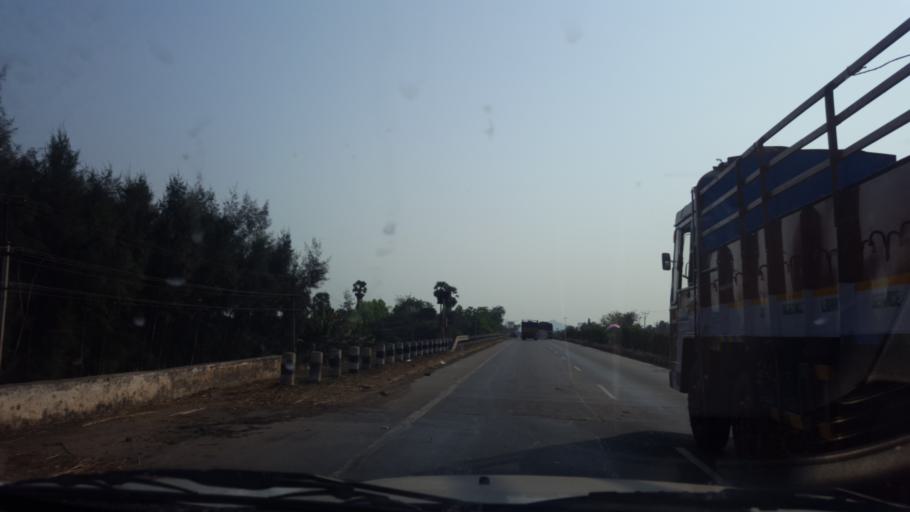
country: IN
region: Andhra Pradesh
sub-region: Vishakhapatnam
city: Elamanchili
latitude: 17.5923
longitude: 82.8712
